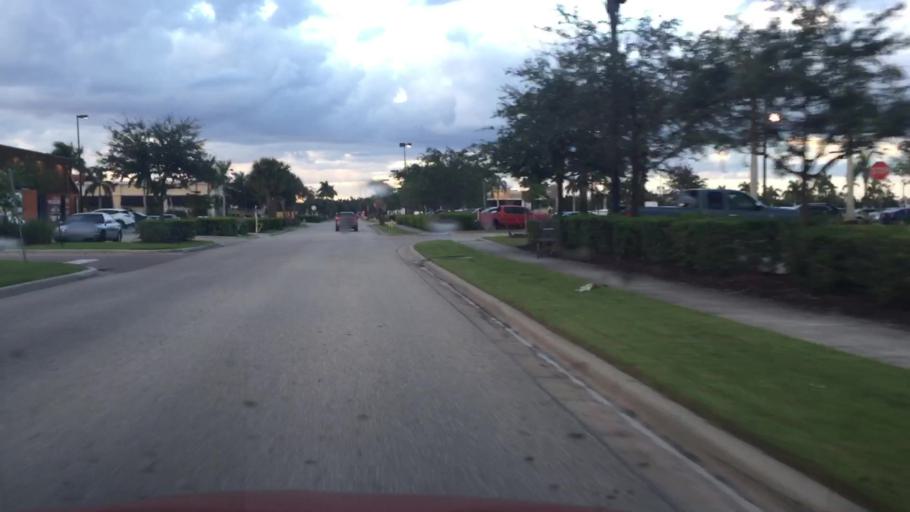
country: US
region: Florida
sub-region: Lee County
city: Fort Myers
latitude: 26.6059
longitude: -81.8100
